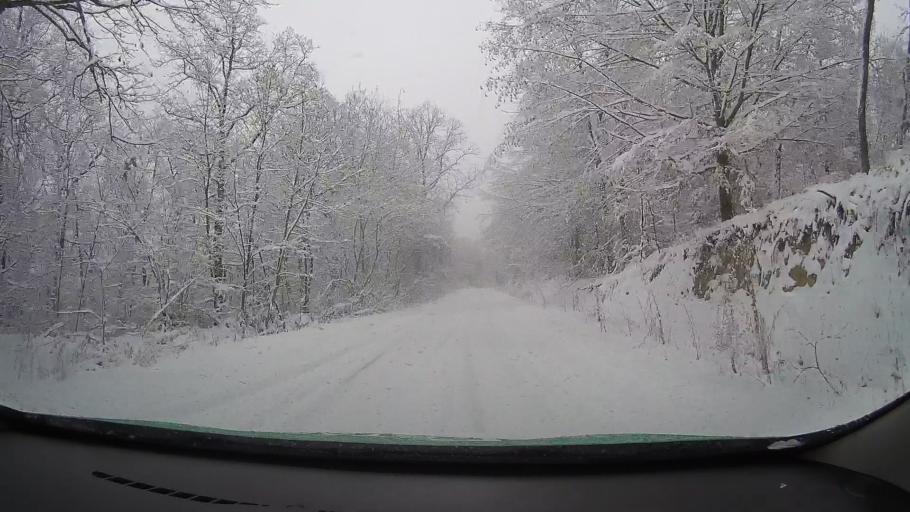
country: RO
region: Hunedoara
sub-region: Comuna Teliucu Inferior
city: Teliucu Inferior
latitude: 45.6894
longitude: 22.8961
